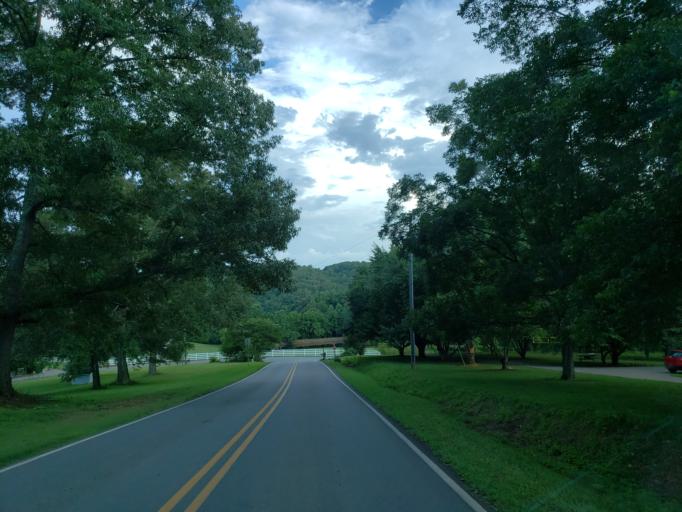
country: US
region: Georgia
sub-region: Cherokee County
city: Ball Ground
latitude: 34.3229
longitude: -84.4246
